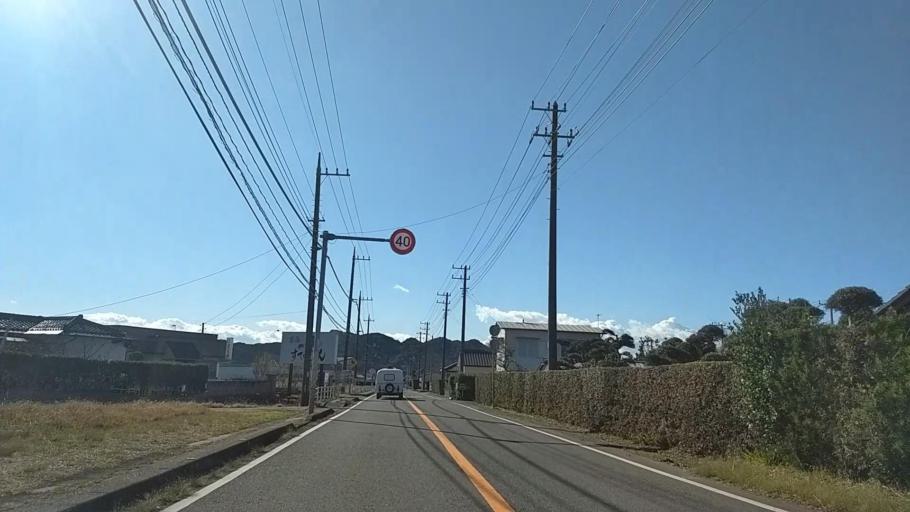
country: JP
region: Chiba
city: Tateyama
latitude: 34.9351
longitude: 139.8402
